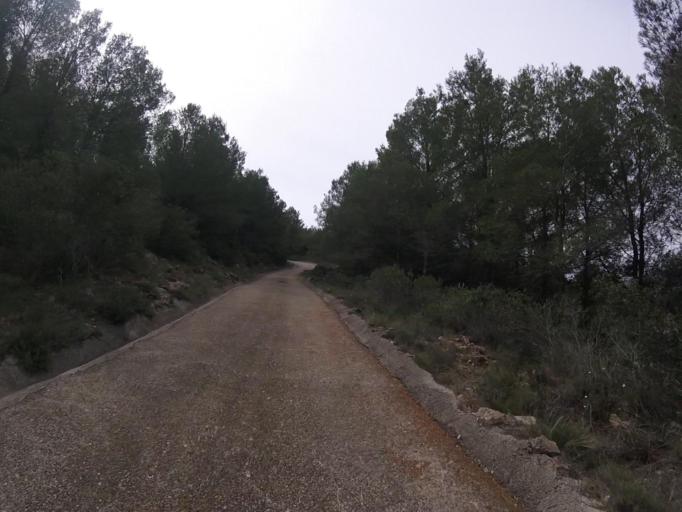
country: ES
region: Valencia
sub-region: Provincia de Castello
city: Cabanes
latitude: 40.1914
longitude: 0.0779
